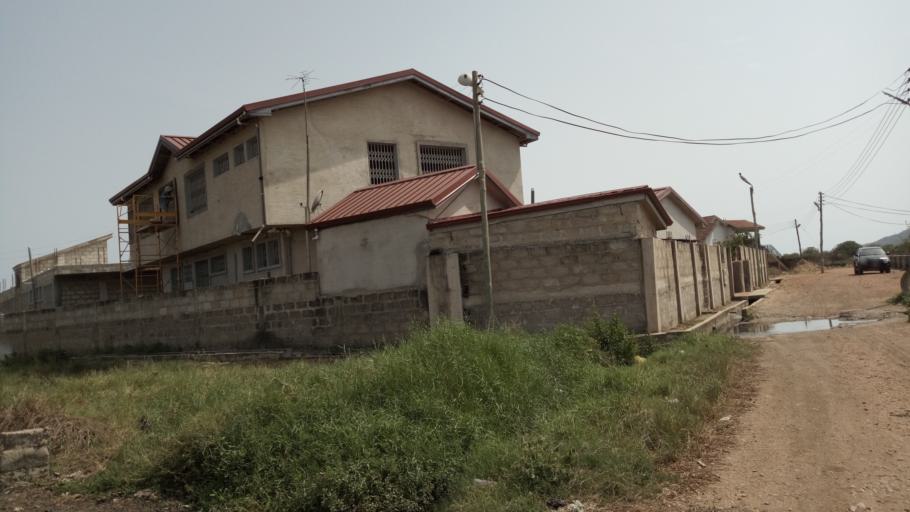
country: GH
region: Central
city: Winneba
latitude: 5.3615
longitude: -0.6379
